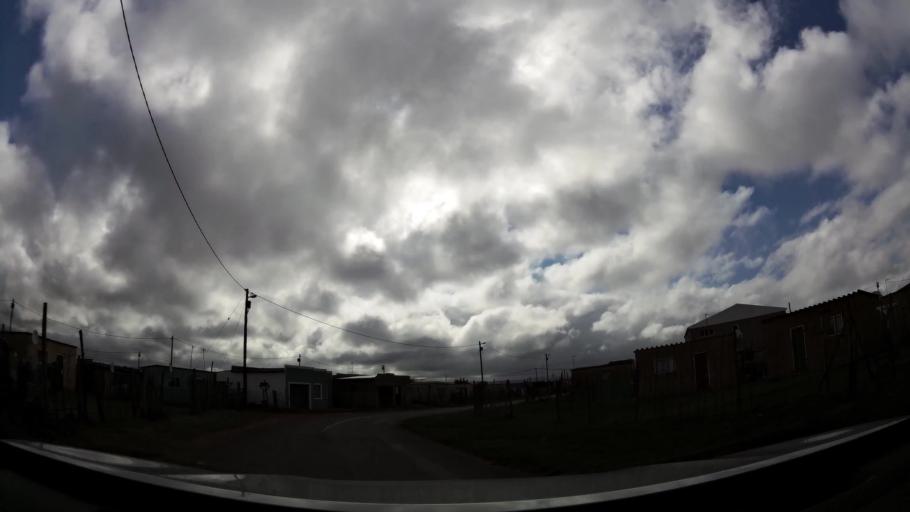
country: ZA
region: Western Cape
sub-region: Eden District Municipality
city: Plettenberg Bay
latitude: -34.0566
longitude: 23.3163
